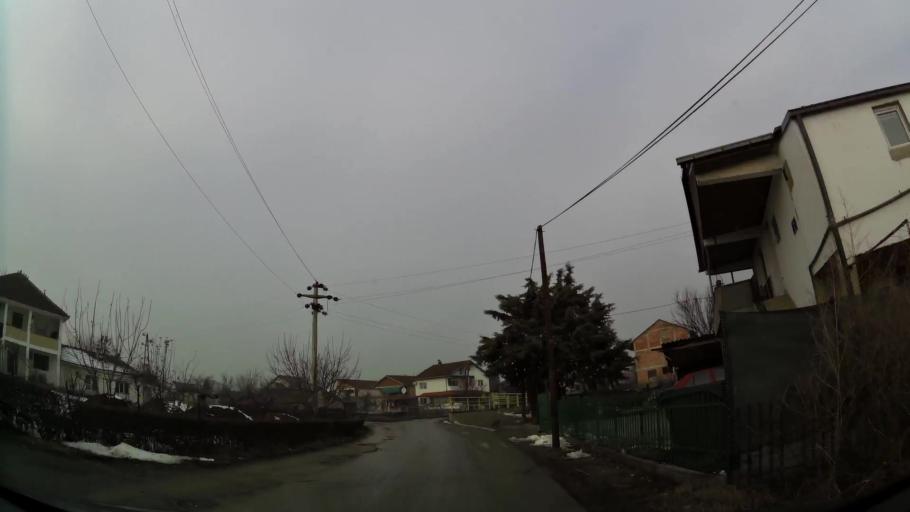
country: MK
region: Ilinden
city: Ilinden
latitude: 41.9944
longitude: 21.5812
